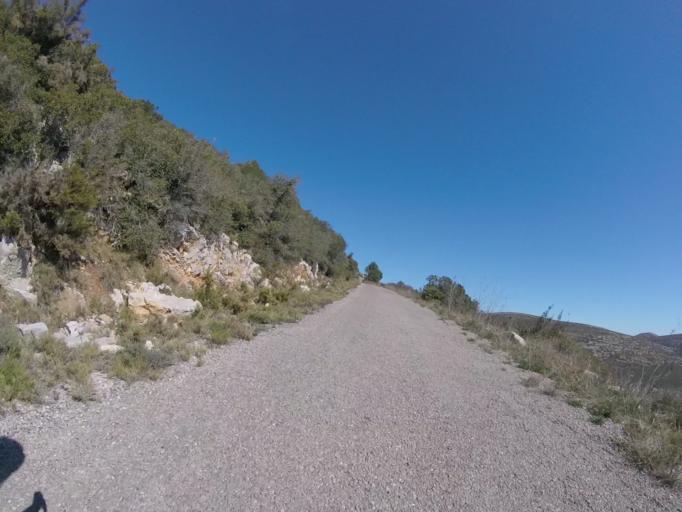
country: ES
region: Valencia
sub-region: Provincia de Castello
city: Cervera del Maestre
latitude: 40.4111
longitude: 0.2016
